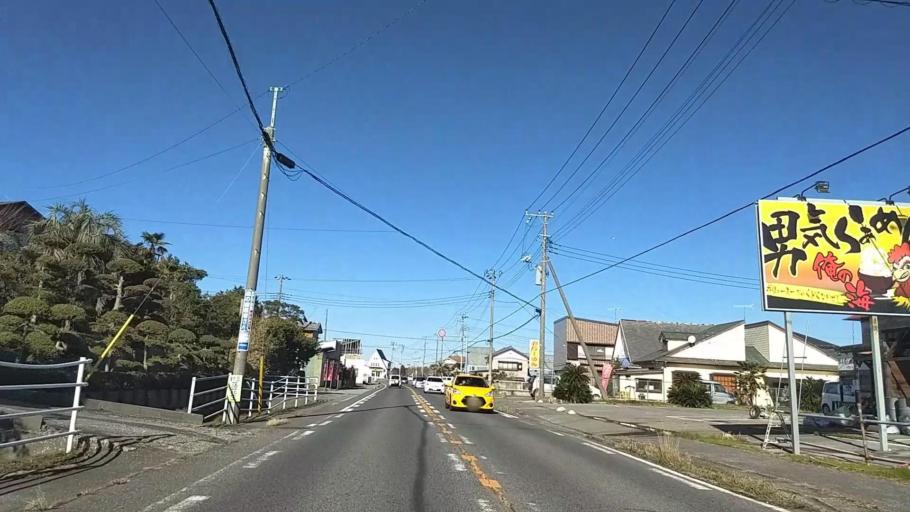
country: JP
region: Chiba
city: Ohara
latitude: 35.2951
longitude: 140.3957
